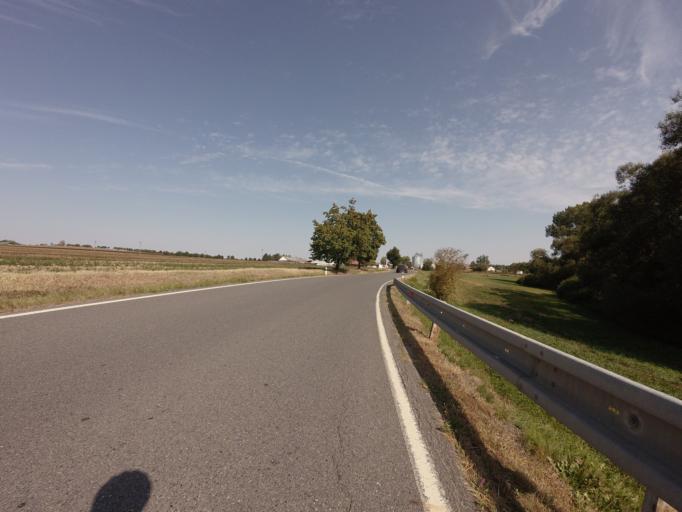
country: CZ
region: Jihocesky
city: Bernartice
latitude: 49.3608
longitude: 14.3770
